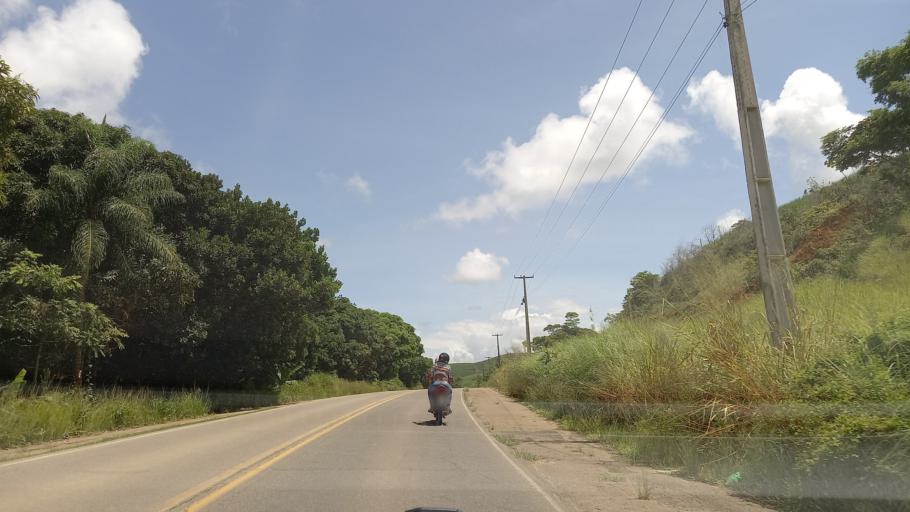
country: BR
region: Pernambuco
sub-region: Sirinhaem
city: Sirinhaem
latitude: -8.6183
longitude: -35.1220
